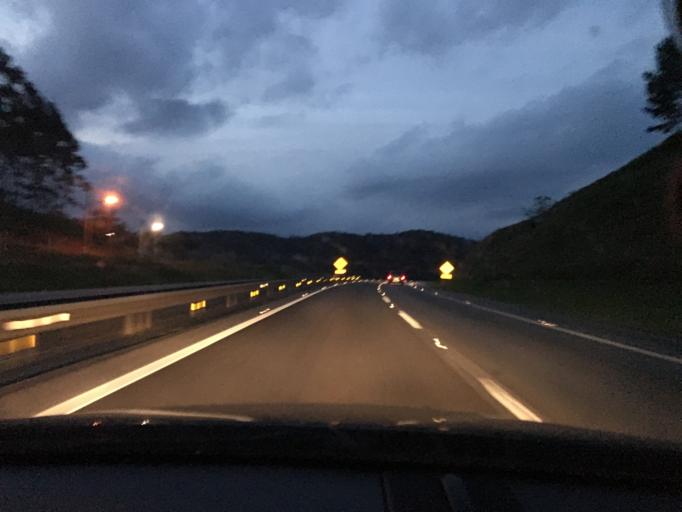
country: BR
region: Sao Paulo
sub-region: Santa Isabel
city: Santa Isabel
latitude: -23.3367
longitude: -46.1307
